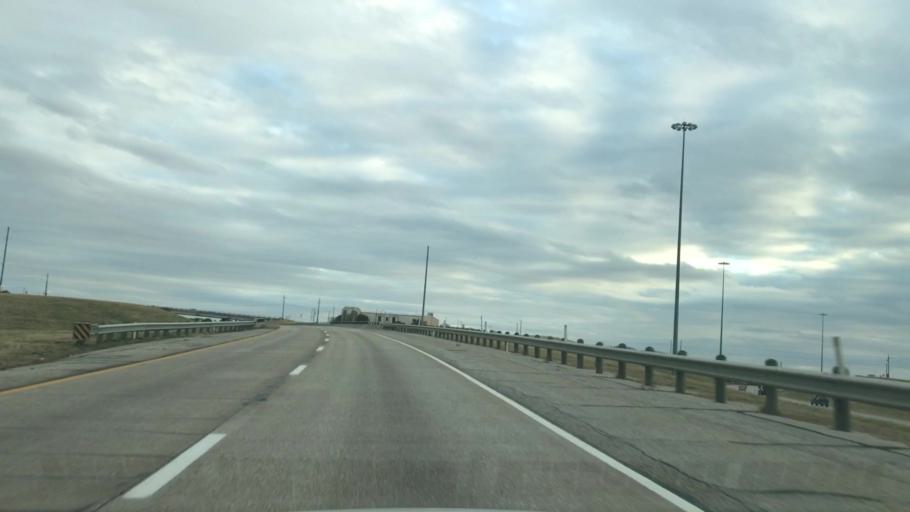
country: US
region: Texas
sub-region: Dallas County
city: Cockrell Hill
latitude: 32.7240
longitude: -96.9184
